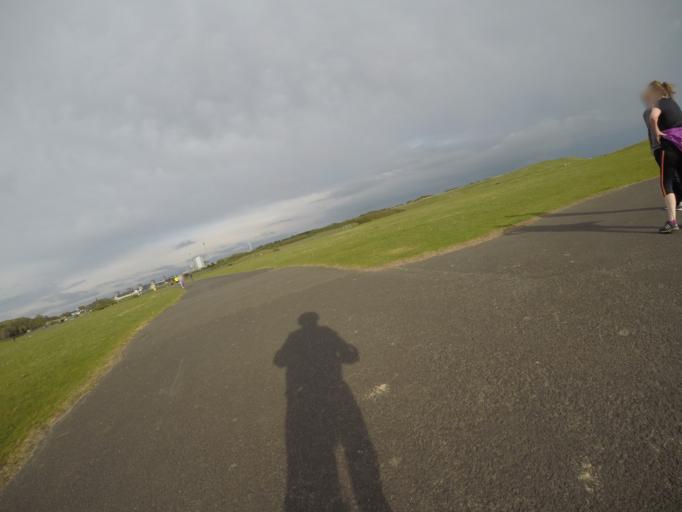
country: GB
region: Scotland
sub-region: North Ayrshire
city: Irvine
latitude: 55.6049
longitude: -4.6911
